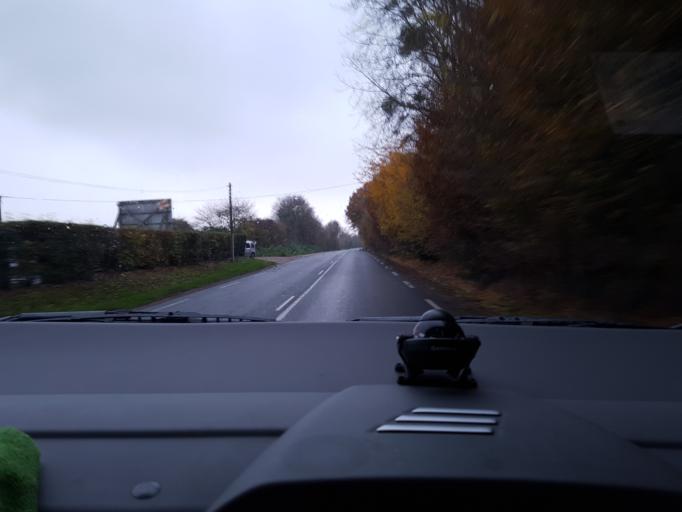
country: FR
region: Lower Normandy
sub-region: Departement du Calvados
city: Saint-Gatien-des-Bois
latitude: 49.2995
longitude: 0.2263
